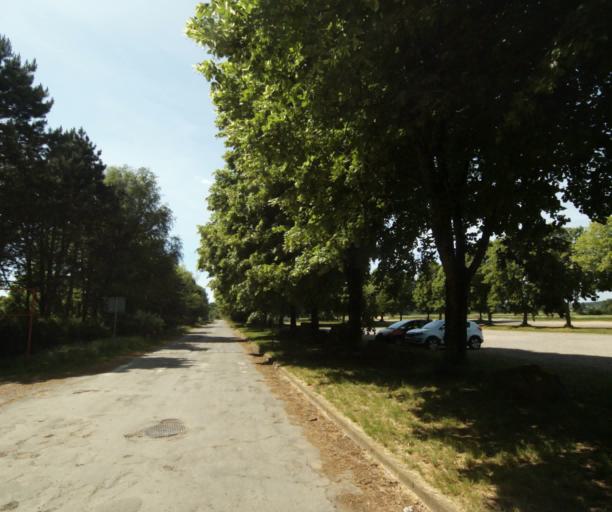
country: FR
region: Champagne-Ardenne
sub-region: Departement des Ardennes
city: Prix-les-Mezieres
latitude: 49.7604
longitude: 4.6855
